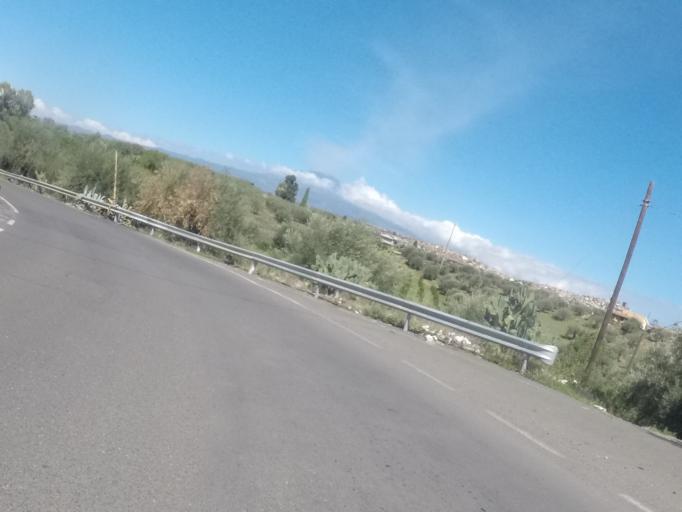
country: IT
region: Sicily
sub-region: Catania
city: Motta Sant'Anastasia
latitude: 37.4972
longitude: 14.9568
